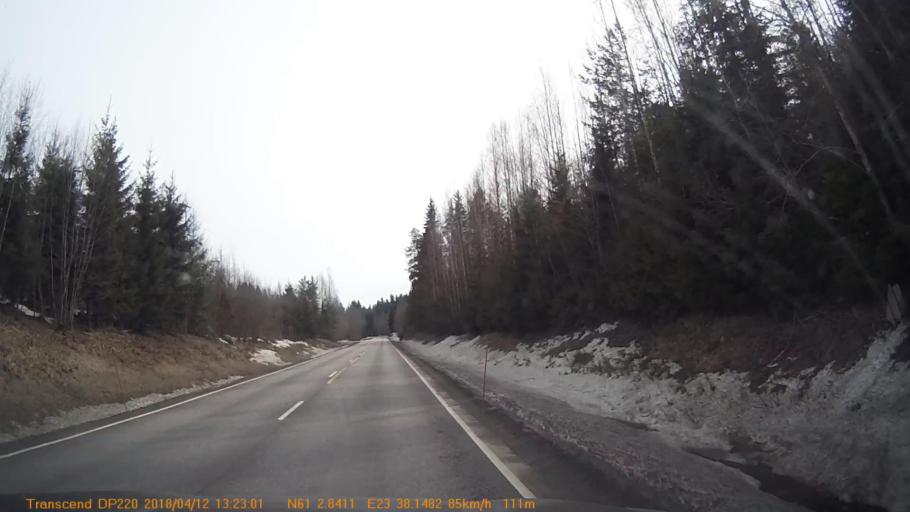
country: FI
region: Pirkanmaa
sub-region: Etelae-Pirkanmaa
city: Urjala
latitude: 61.0463
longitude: 23.6368
